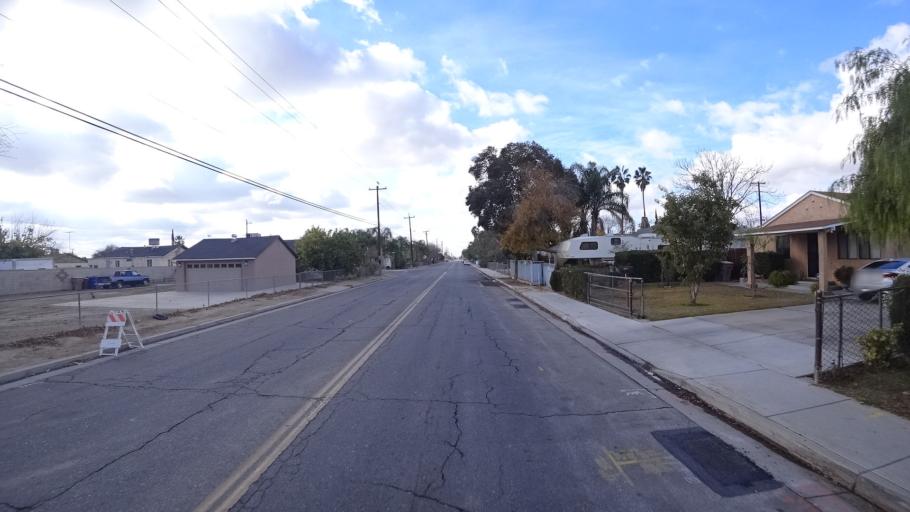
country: US
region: California
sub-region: Kern County
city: Bakersfield
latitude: 35.3614
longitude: -118.9594
